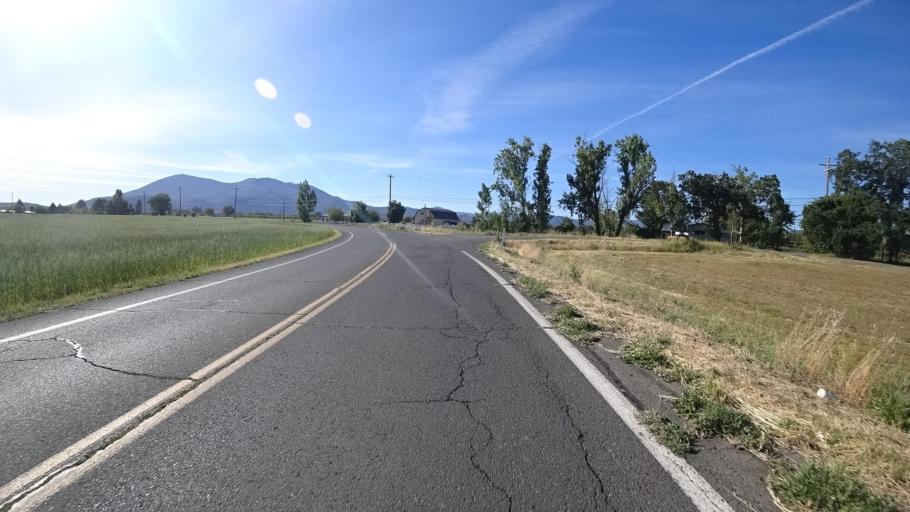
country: US
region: California
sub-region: Lake County
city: Kelseyville
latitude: 39.0119
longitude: -122.8567
